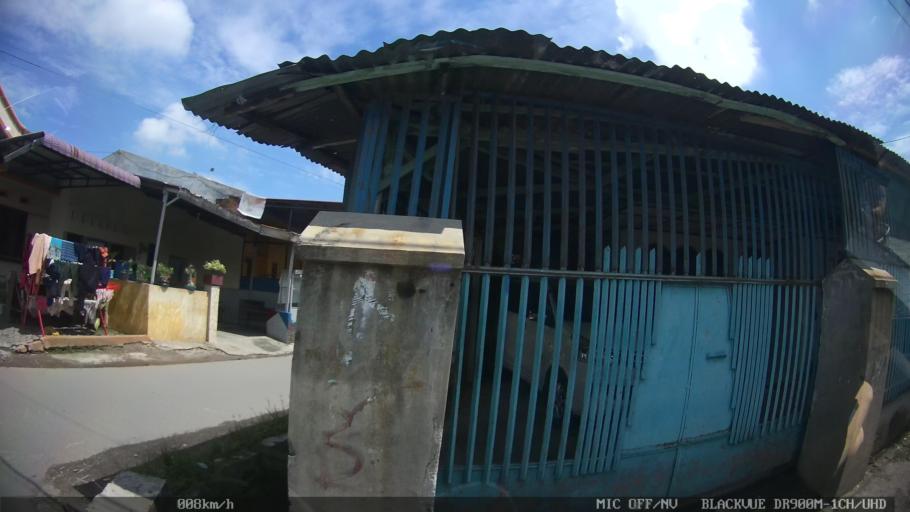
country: ID
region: North Sumatra
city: Medan
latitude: 3.6021
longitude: 98.7561
